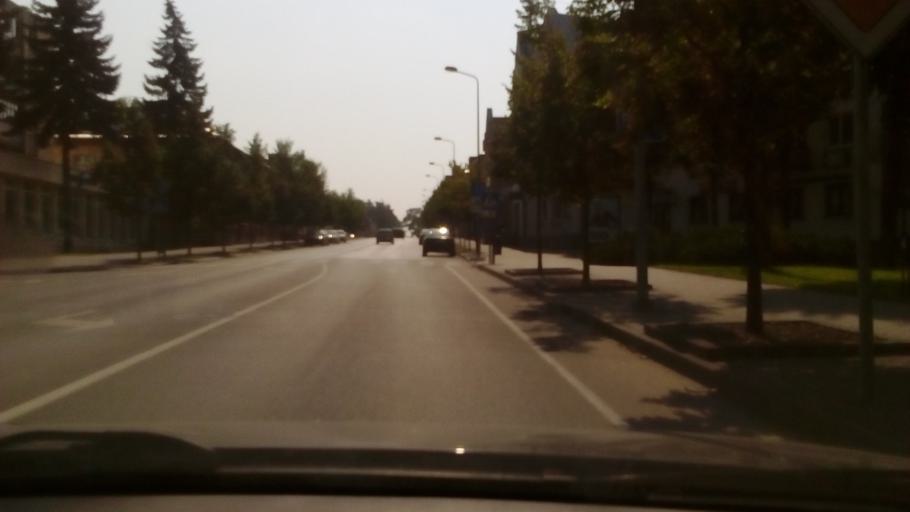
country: LT
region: Alytaus apskritis
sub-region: Alytus
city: Alytus
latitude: 54.3987
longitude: 24.0483
